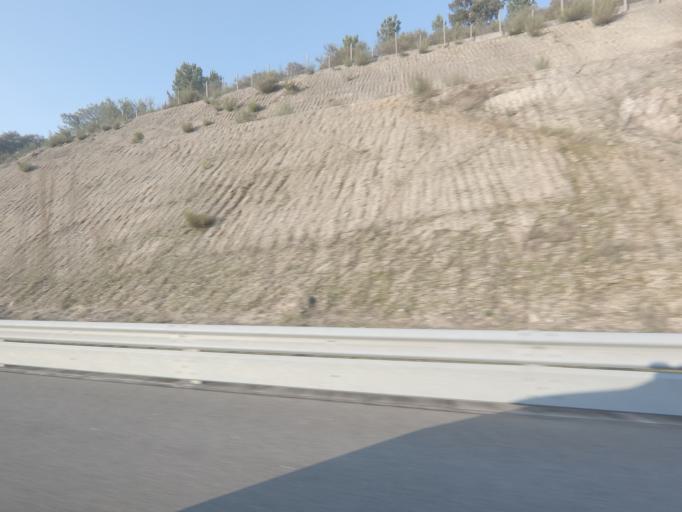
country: PT
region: Porto
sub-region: Amarante
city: Amarante
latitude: 41.2553
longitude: -8.0396
